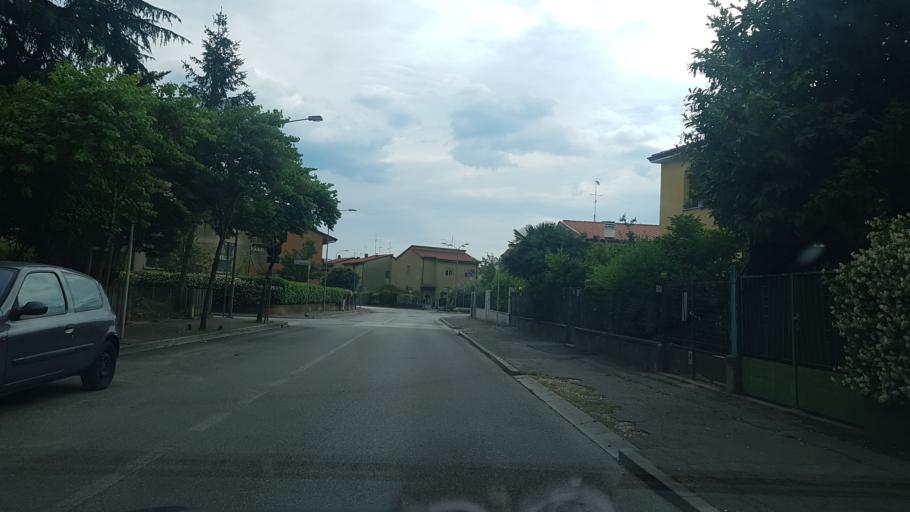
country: IT
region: Friuli Venezia Giulia
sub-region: Provincia di Gorizia
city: Gorizia
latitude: 45.9298
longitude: 13.6160
